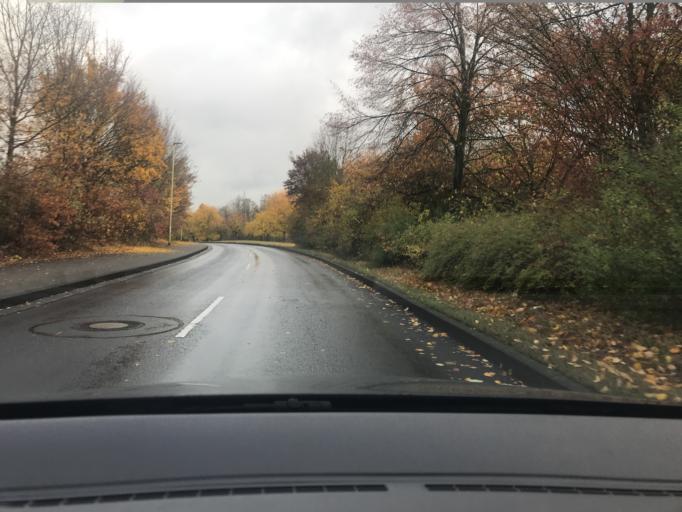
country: DE
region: Hesse
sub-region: Regierungsbezirk Darmstadt
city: Friedberg
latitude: 50.3209
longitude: 8.7684
